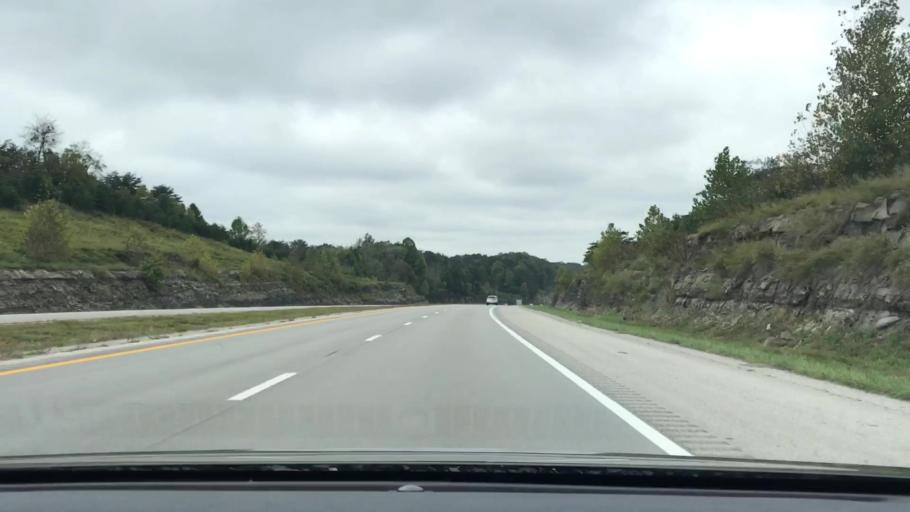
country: US
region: Kentucky
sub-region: Pulaski County
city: Somerset
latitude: 37.1008
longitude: -84.6700
